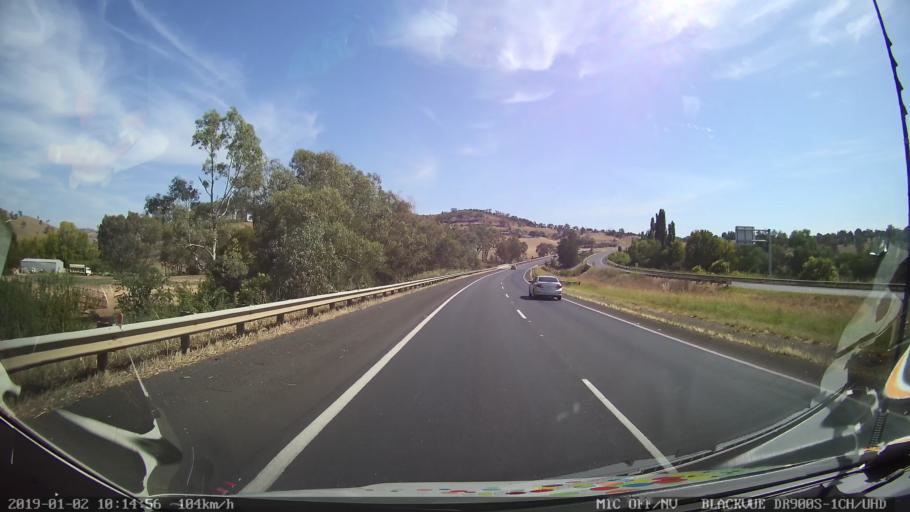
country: AU
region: New South Wales
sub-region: Gundagai
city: Gundagai
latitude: -35.0567
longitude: 148.0948
